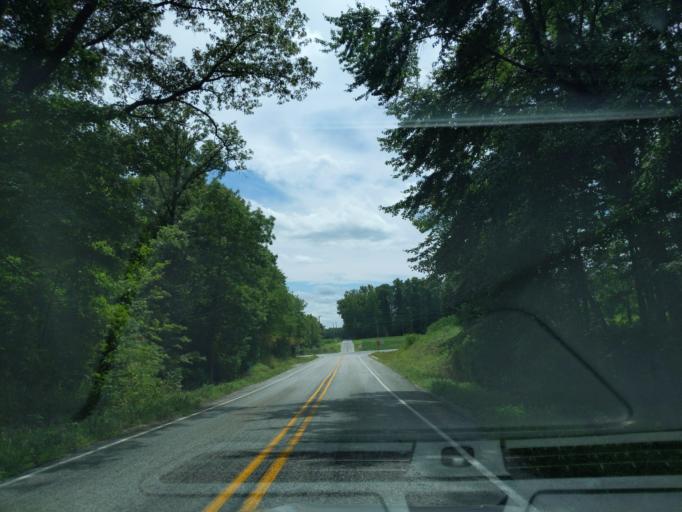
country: US
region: Indiana
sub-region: Ripley County
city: Osgood
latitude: 39.1975
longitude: -85.2776
